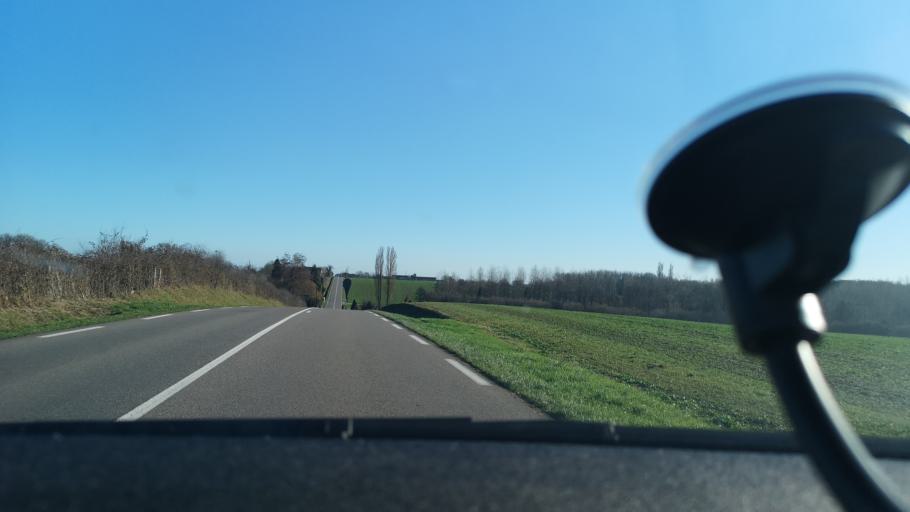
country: FR
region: Bourgogne
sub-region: Departement de Saone-et-Loire
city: Saint-Martin-en-Bresse
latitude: 46.7498
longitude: 5.0402
